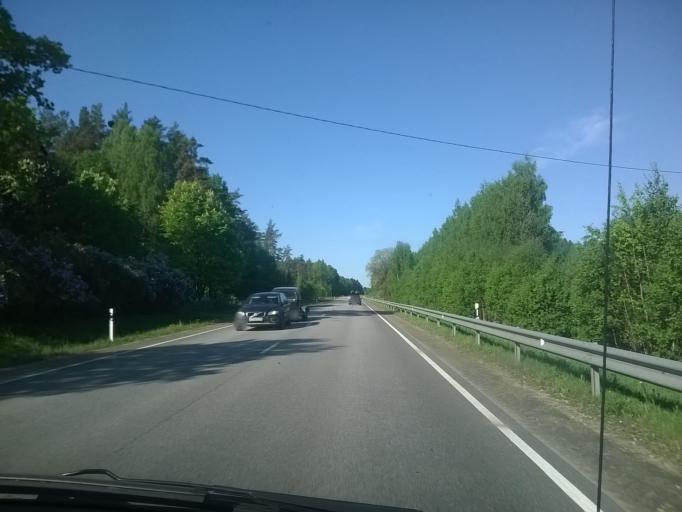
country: LV
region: Beverina
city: Murmuiza
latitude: 57.5928
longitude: 25.5545
